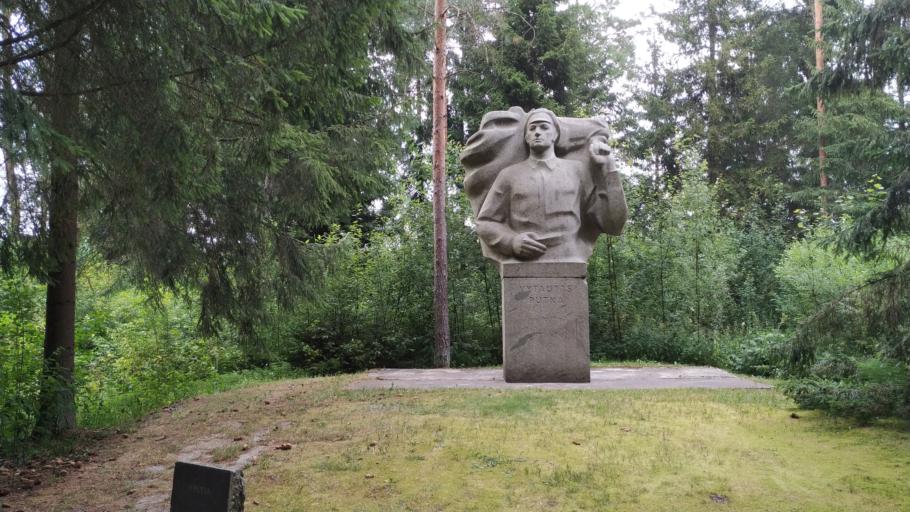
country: LT
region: Alytaus apskritis
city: Druskininkai
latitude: 54.0215
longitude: 24.0817
